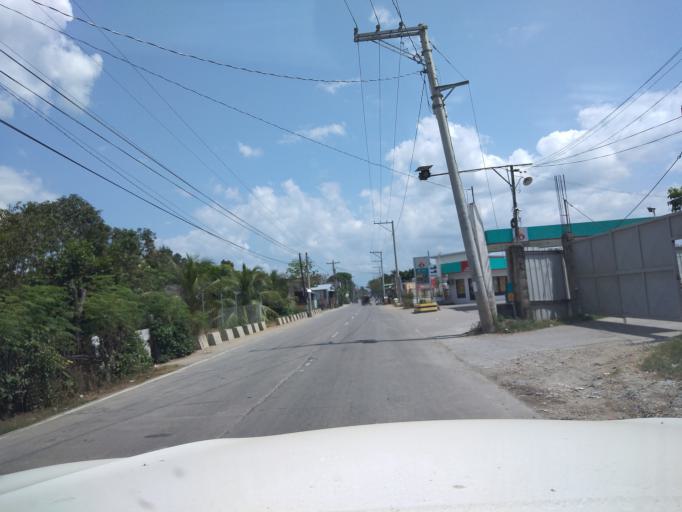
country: PH
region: Central Luzon
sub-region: Province of Pampanga
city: Lourdes
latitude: 15.0189
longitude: 120.8652
